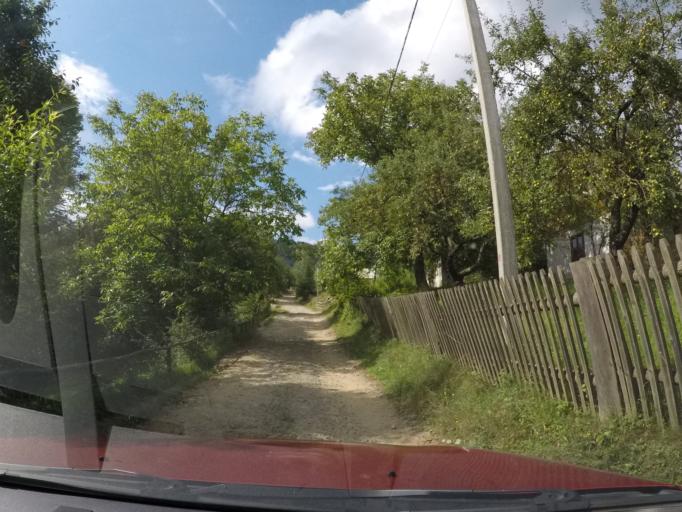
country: UA
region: Zakarpattia
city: Velykyi Bereznyi
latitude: 48.9461
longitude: 22.6767
